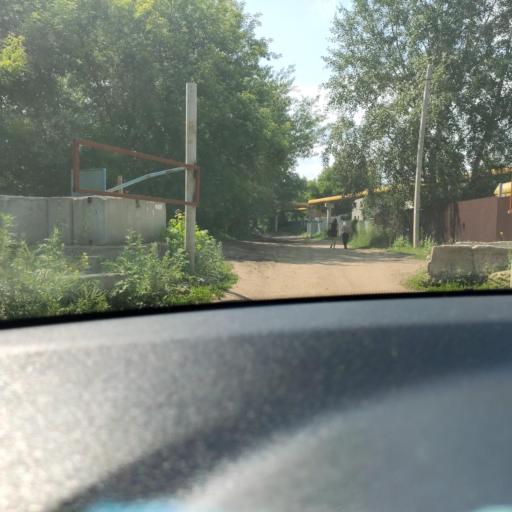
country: RU
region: Samara
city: Smyshlyayevka
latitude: 53.2152
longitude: 50.3346
